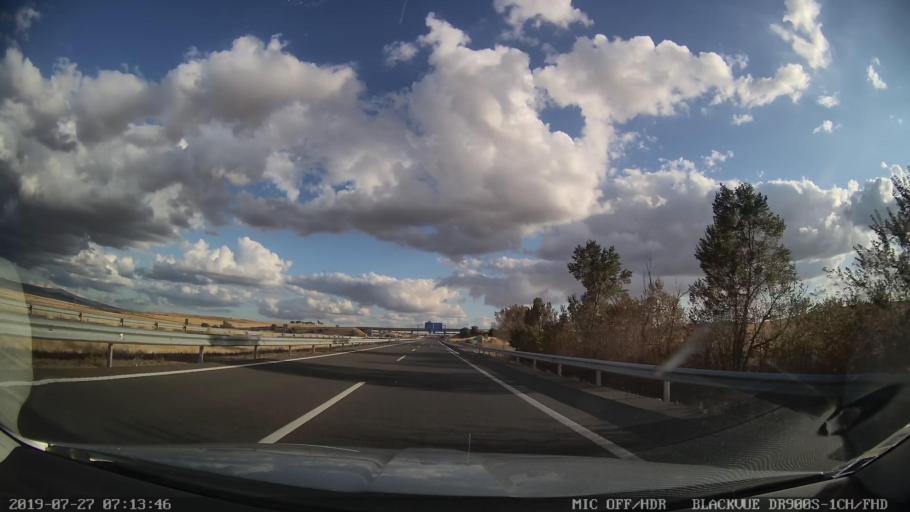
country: ES
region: Extremadura
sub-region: Provincia de Caceres
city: Trujillo
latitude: 39.5056
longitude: -5.8388
